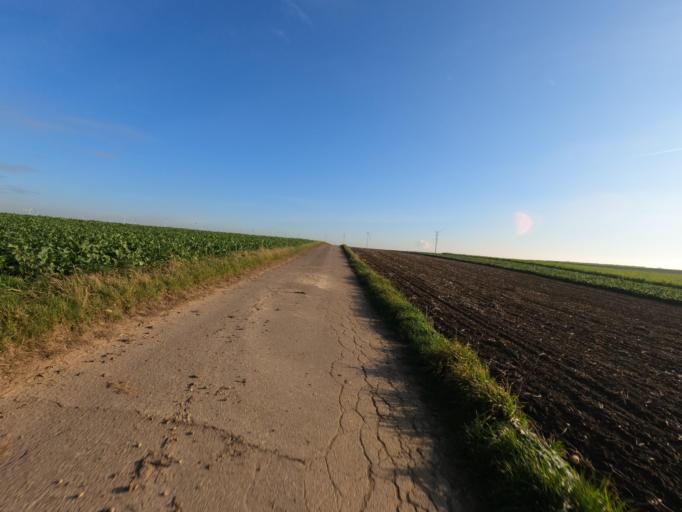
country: DE
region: North Rhine-Westphalia
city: Huckelhoven
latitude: 50.9912
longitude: 6.1955
